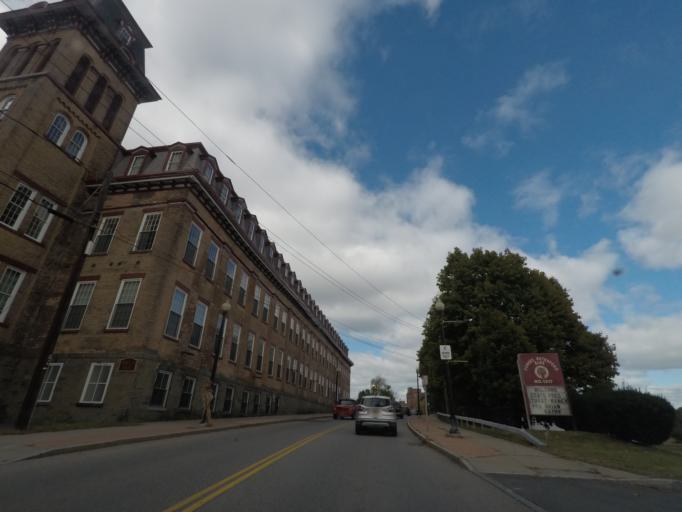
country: US
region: New York
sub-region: Albany County
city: Cohoes
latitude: 42.7784
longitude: -73.7021
